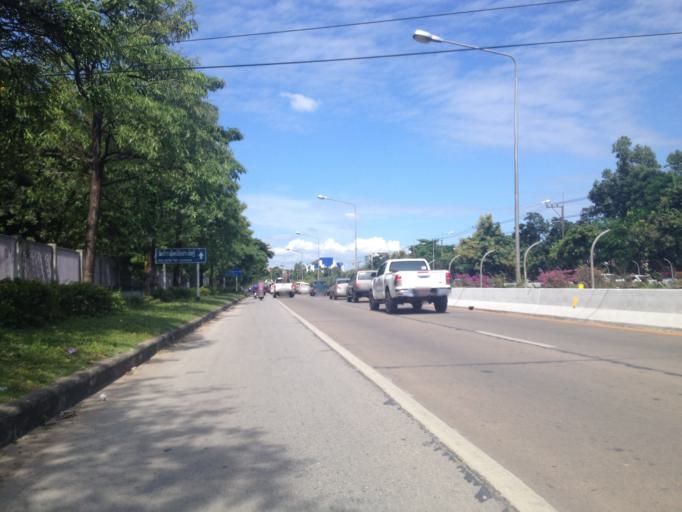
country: TH
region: Chiang Mai
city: Chiang Mai
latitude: 18.7928
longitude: 98.9612
